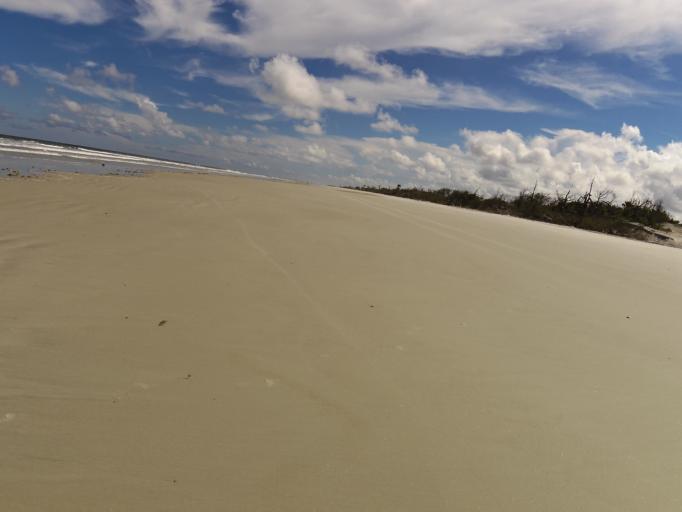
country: US
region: Florida
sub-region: Duval County
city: Atlantic Beach
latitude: 30.4731
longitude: -81.4127
